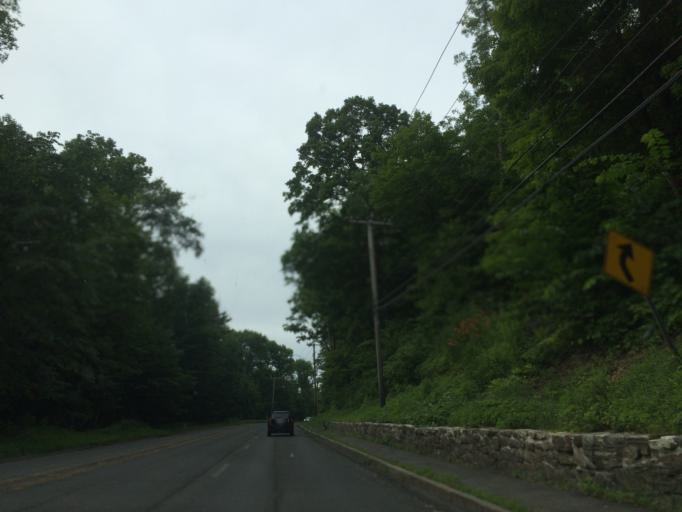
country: US
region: Massachusetts
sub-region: Berkshire County
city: Pittsfield
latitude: 42.4209
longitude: -73.2606
